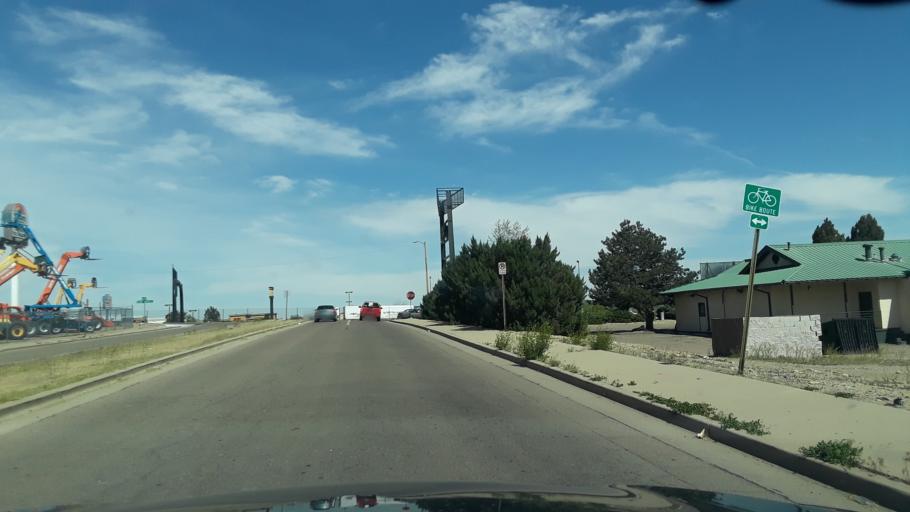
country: US
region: Colorado
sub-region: Pueblo County
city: Pueblo
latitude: 38.3118
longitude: -104.6166
